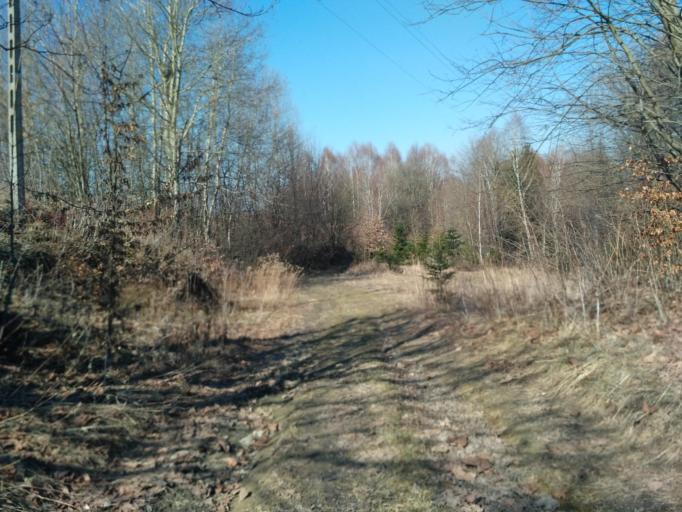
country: PL
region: Subcarpathian Voivodeship
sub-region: Powiat brzozowski
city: Golcowa
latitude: 49.7558
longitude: 22.0346
